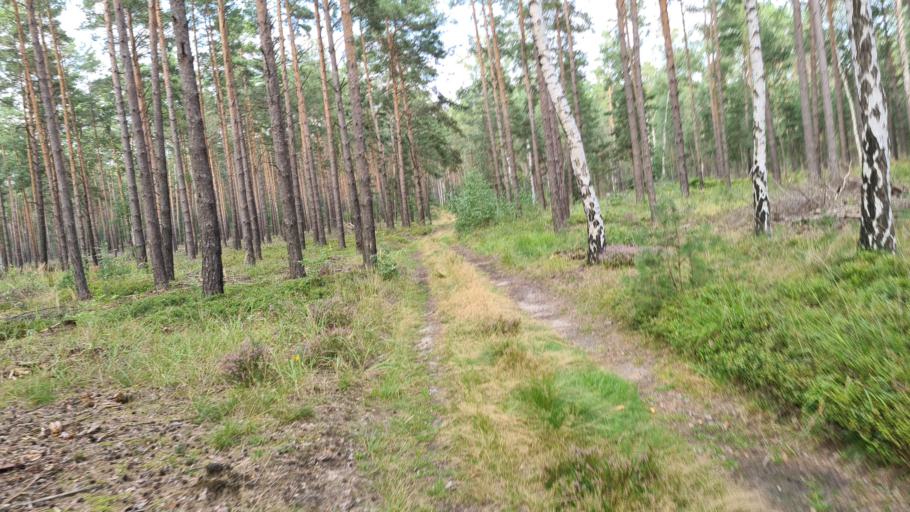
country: DE
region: Brandenburg
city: Trobitz
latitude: 51.6081
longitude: 13.4362
